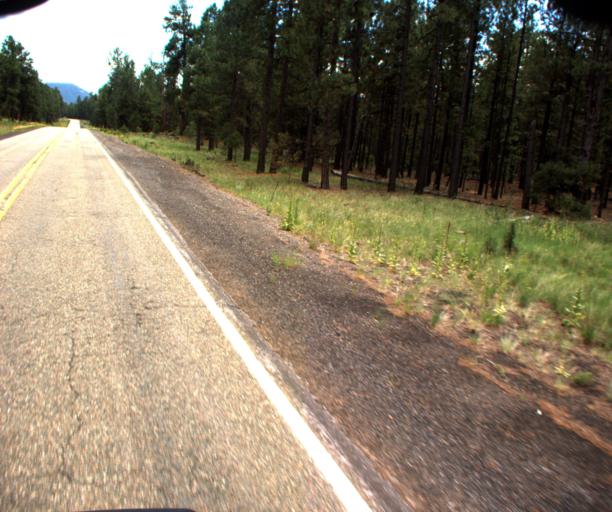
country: US
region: Arizona
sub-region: Coconino County
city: Flagstaff
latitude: 35.2946
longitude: -111.7649
